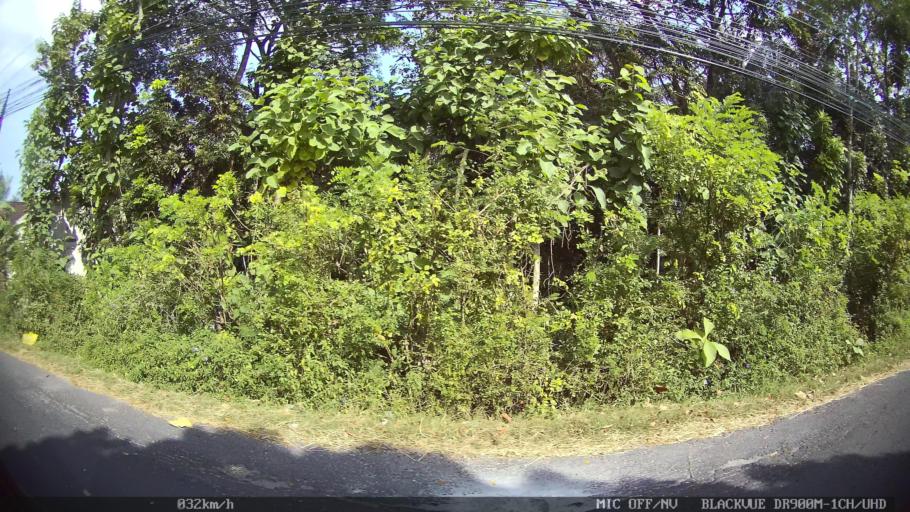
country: ID
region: Daerah Istimewa Yogyakarta
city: Kasihan
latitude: -7.8420
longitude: 110.3063
